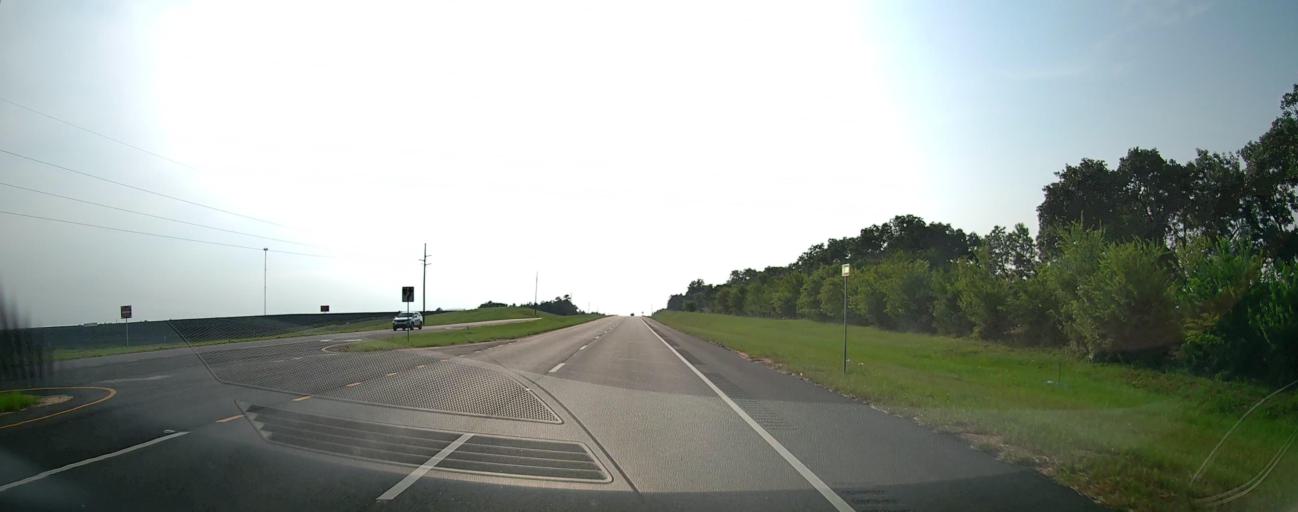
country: US
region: Georgia
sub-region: Taylor County
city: Butler
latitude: 32.5785
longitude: -84.3148
